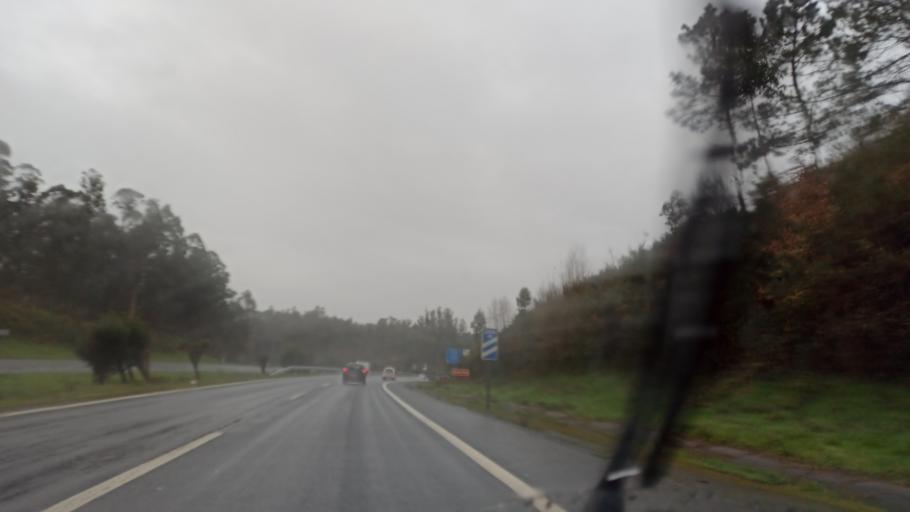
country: ES
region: Galicia
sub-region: Provincia da Coruna
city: Betanzos
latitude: 43.2612
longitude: -8.2222
